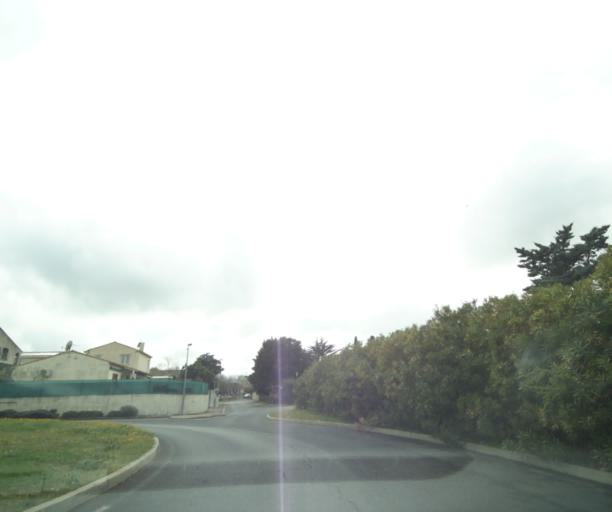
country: FR
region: Languedoc-Roussillon
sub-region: Departement de l'Herault
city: Saussan
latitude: 43.5680
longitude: 3.7740
